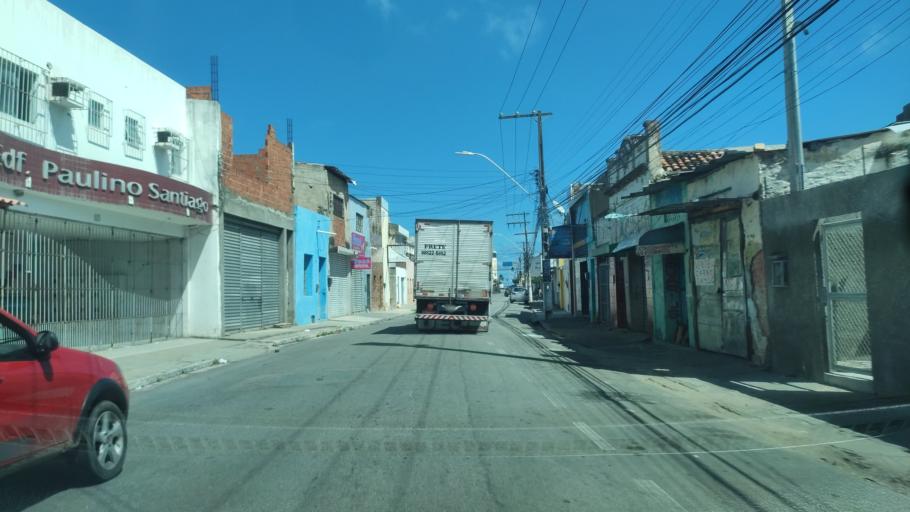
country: BR
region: Alagoas
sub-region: Maceio
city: Maceio
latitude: -9.6656
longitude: -35.7420
